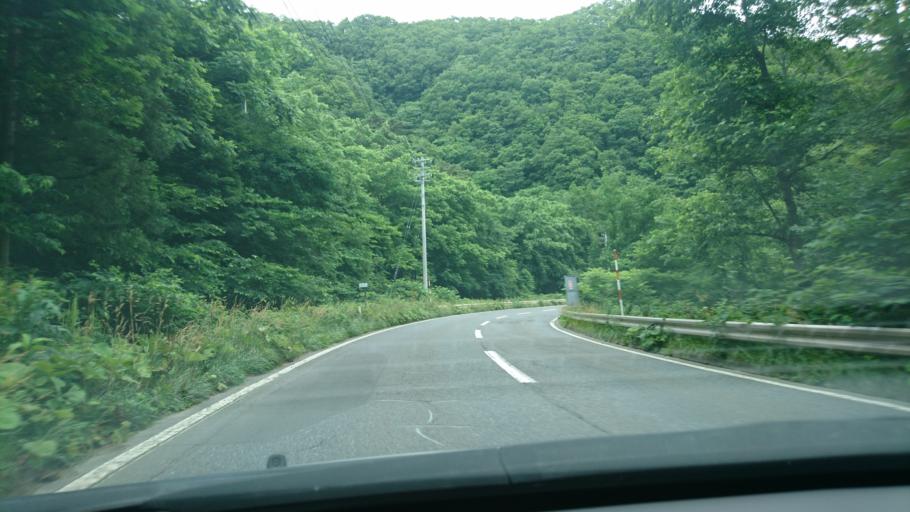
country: JP
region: Iwate
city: Miyako
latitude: 39.9872
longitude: 141.8634
